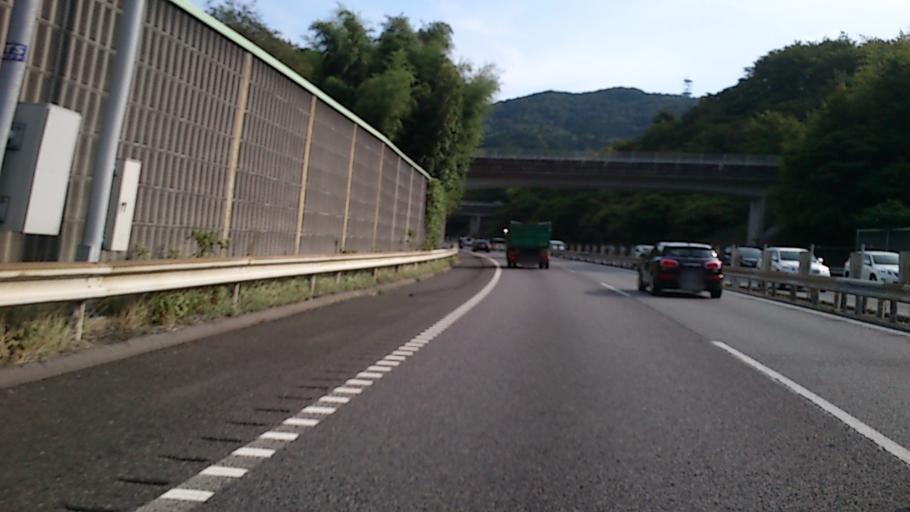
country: JP
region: Shiga Prefecture
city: Otsu-shi
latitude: 34.9456
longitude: 135.8889
